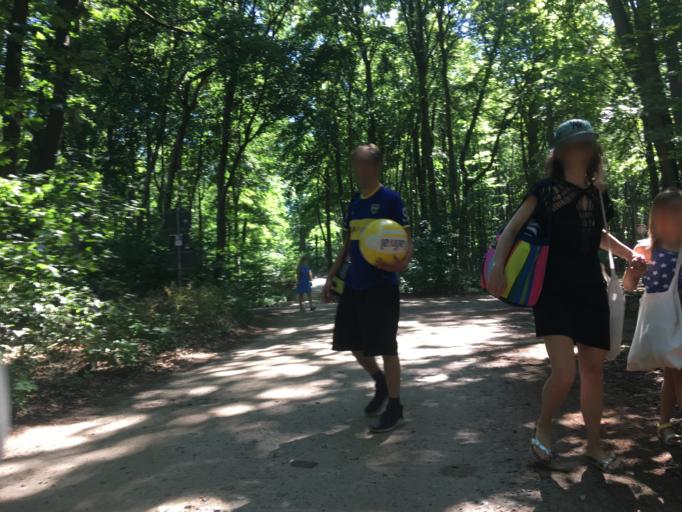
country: DE
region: Brandenburg
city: Grosswoltersdorf
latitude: 53.1506
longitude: 13.0427
